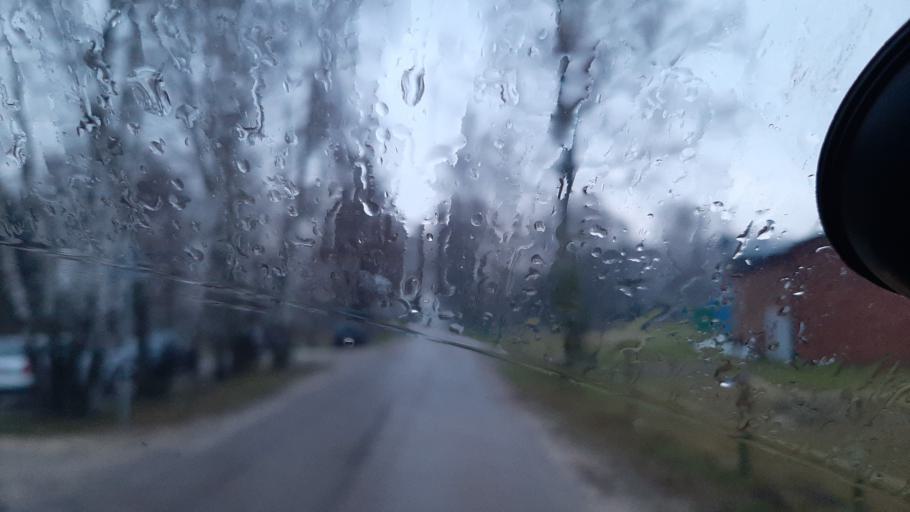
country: PL
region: Lublin Voivodeship
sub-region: Powiat lubartowski
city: Firlej
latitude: 51.5571
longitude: 22.5243
